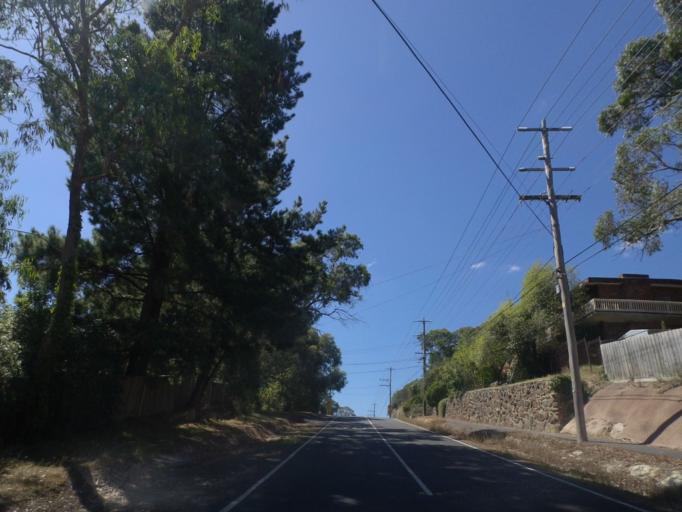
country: AU
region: Victoria
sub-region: Manningham
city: Park Orchards
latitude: -37.7998
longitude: 145.2157
